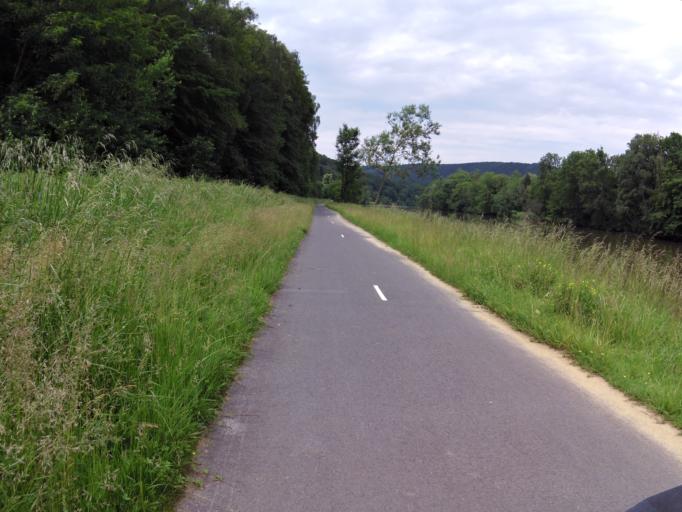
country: FR
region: Champagne-Ardenne
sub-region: Departement des Ardennes
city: Nouzonville
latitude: 49.8045
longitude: 4.7480
